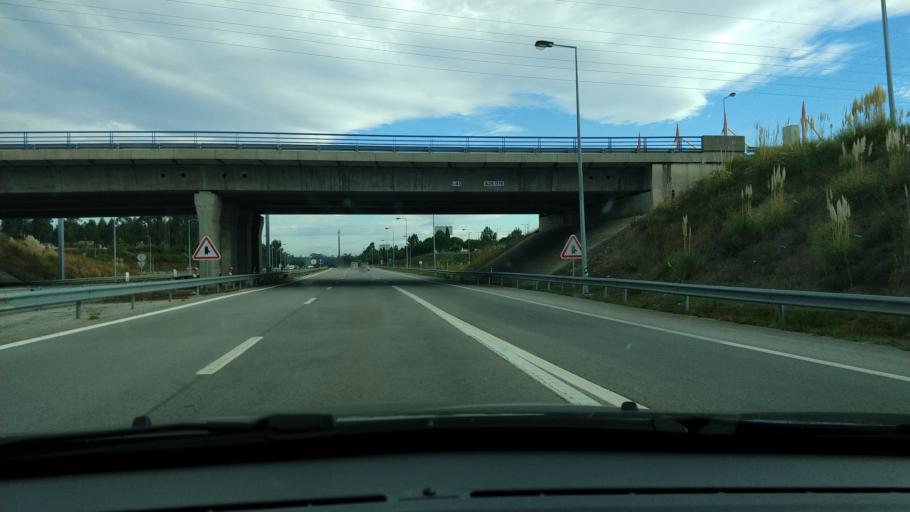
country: PT
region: Aveiro
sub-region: Aveiro
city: Eixo
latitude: 40.6461
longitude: -8.5975
